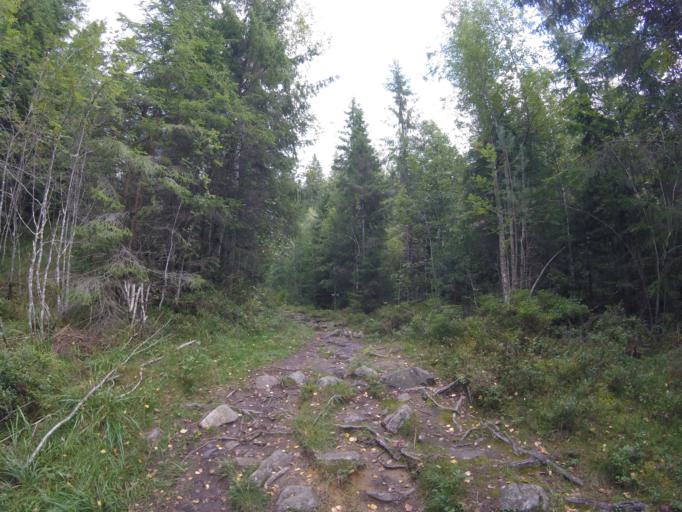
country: NO
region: Akershus
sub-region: Raelingen
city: Fjerdingby
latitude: 59.9097
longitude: 11.0377
